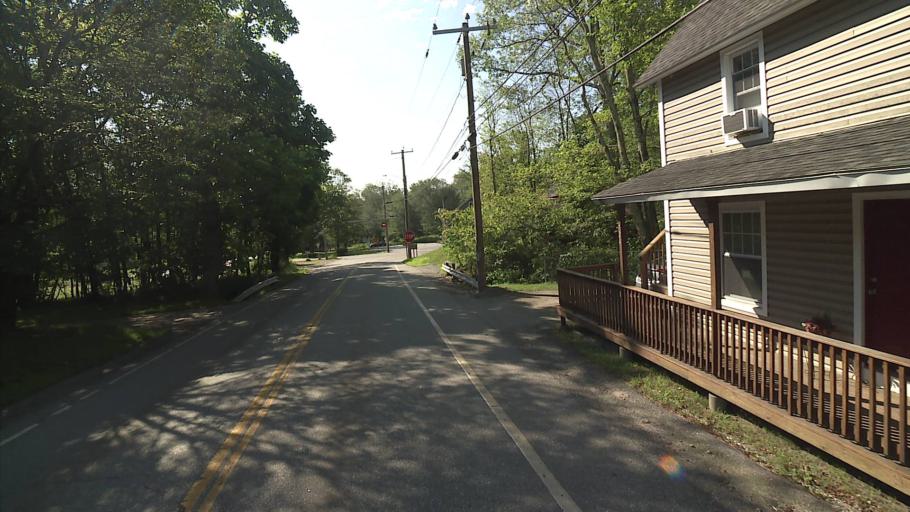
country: US
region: Connecticut
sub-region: New London County
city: Montville Center
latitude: 41.4667
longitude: -72.1588
